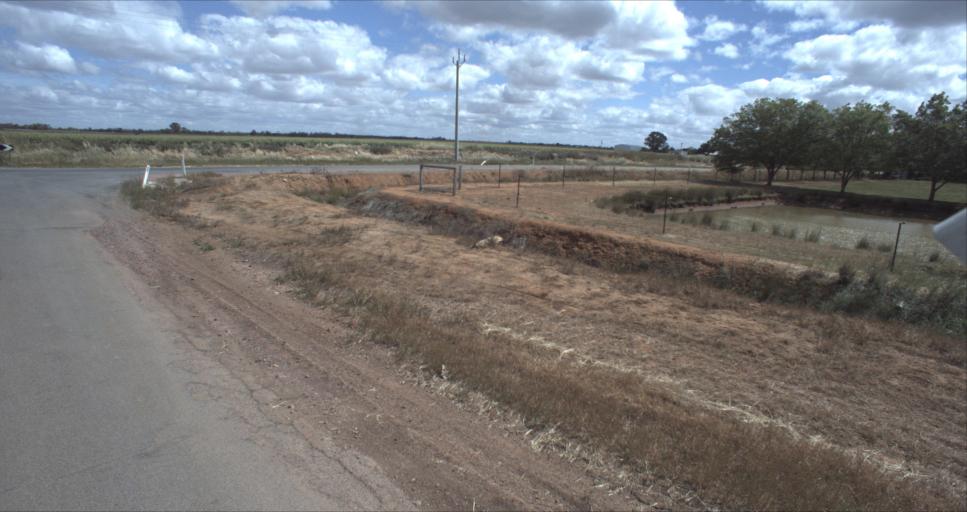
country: AU
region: New South Wales
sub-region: Leeton
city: Leeton
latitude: -34.5894
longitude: 146.3954
